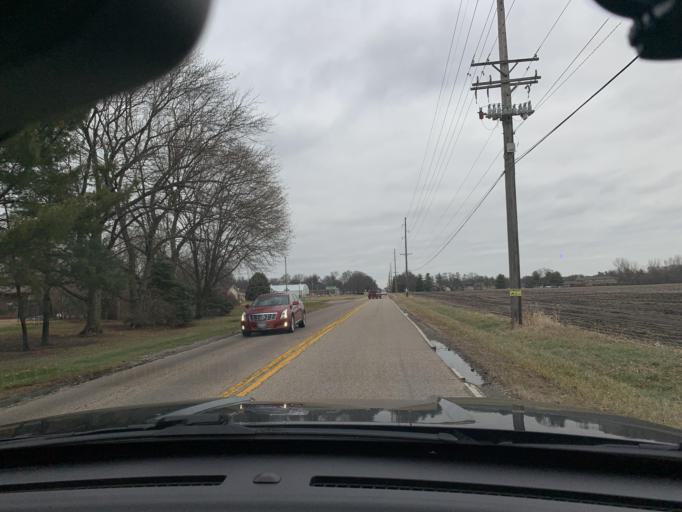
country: US
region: Illinois
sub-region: Sangamon County
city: Jerome
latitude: 39.7526
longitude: -89.6866
